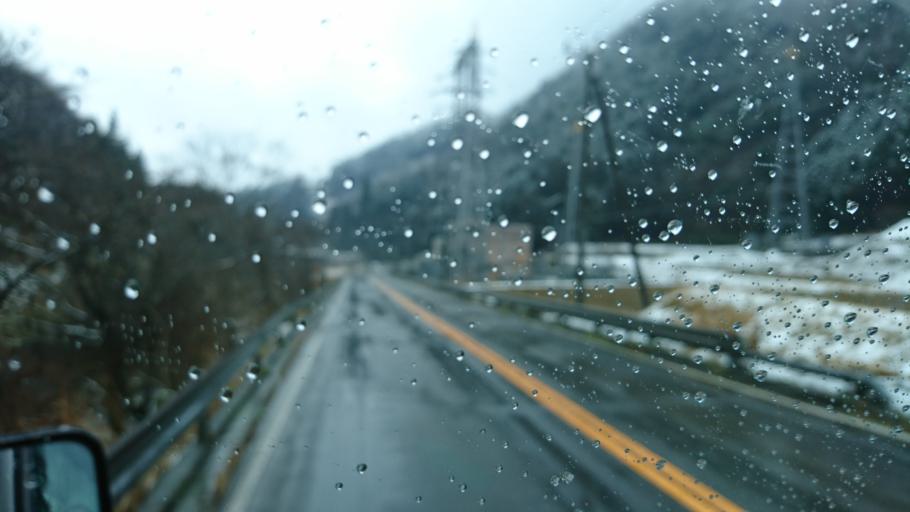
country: JP
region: Tottori
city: Tottori
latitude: 35.5412
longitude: 134.5074
